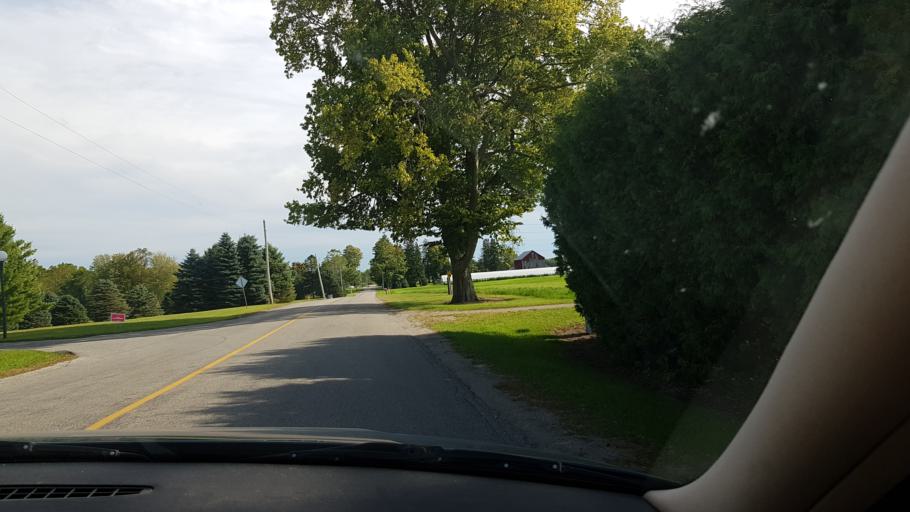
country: CA
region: Ontario
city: Delaware
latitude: 42.8974
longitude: -81.4722
